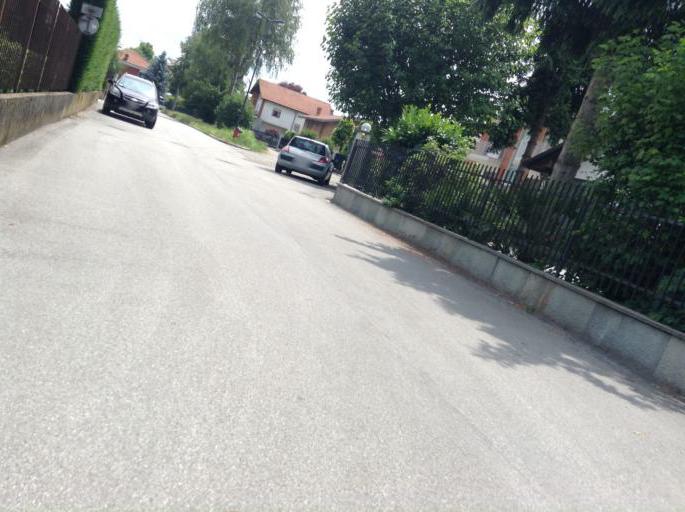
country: IT
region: Piedmont
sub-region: Provincia di Torino
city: Carignano
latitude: 44.9153
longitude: 7.6752
